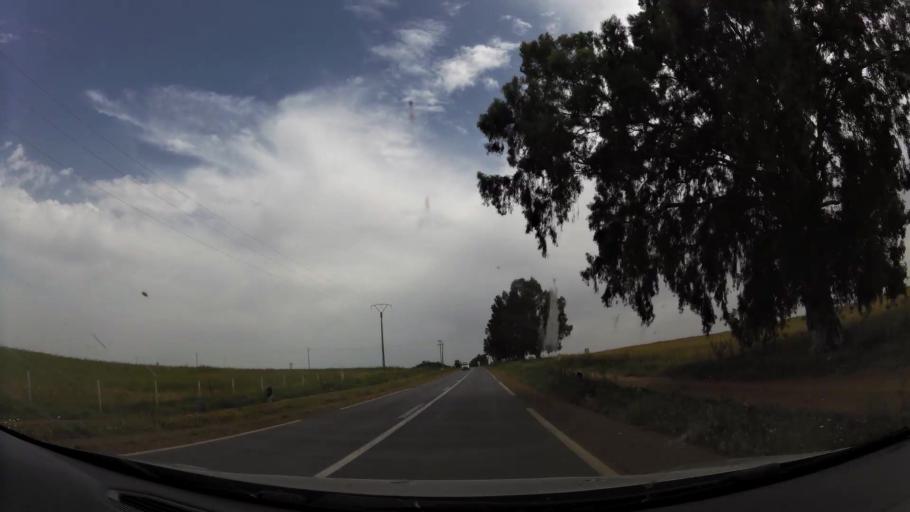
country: MA
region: Rabat-Sale-Zemmour-Zaer
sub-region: Khemisset
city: Tiflet
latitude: 33.8074
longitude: -6.2726
